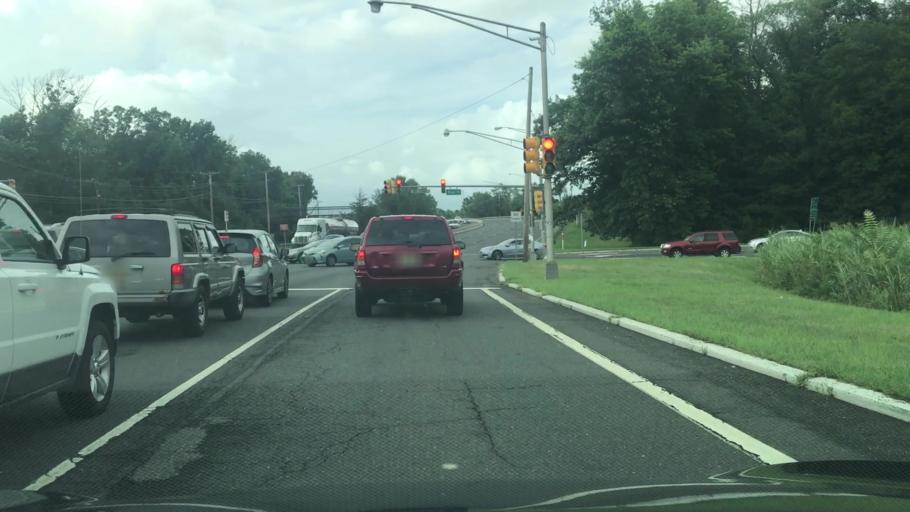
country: US
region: New Jersey
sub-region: Somerset County
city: Bedminster
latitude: 40.6622
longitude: -74.6453
